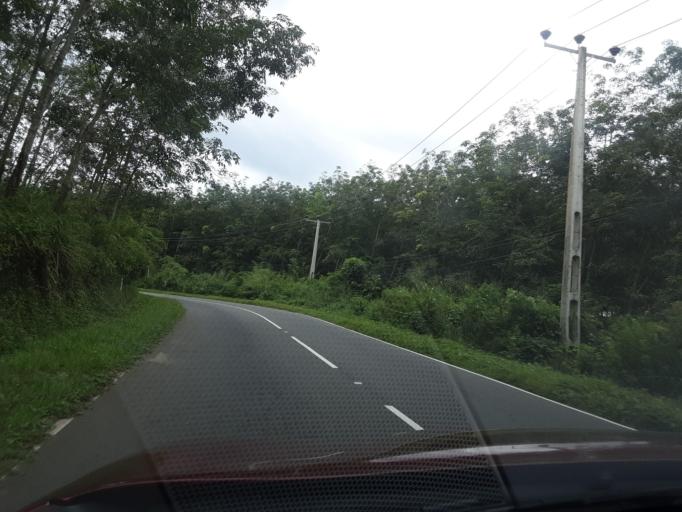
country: LK
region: Uva
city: Monaragala
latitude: 6.9025
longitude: 81.2180
